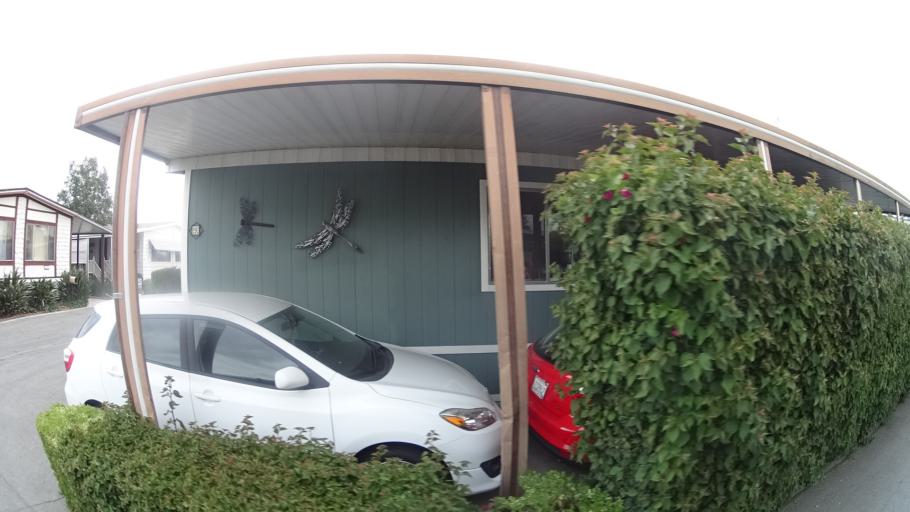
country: US
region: California
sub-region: Los Angeles County
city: San Fernando
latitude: 34.2683
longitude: -118.4694
